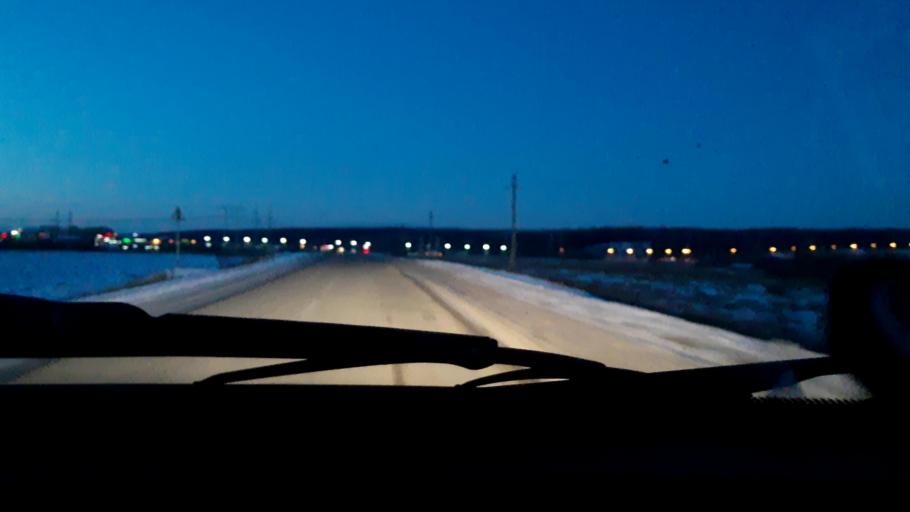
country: RU
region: Bashkortostan
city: Iglino
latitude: 54.7538
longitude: 56.3999
